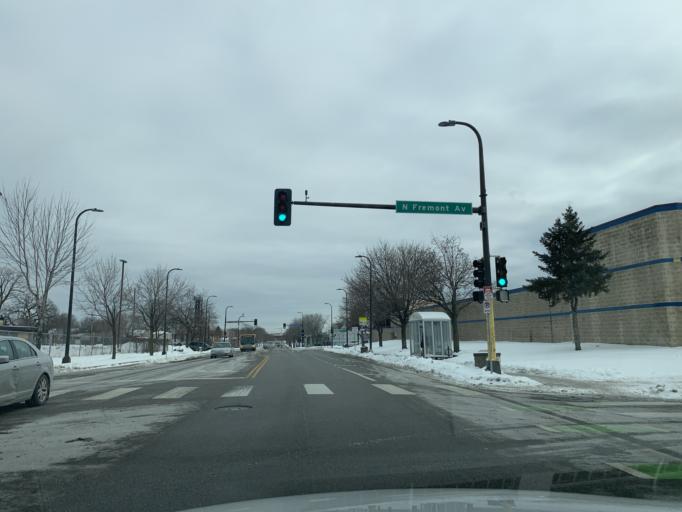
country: US
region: Minnesota
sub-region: Hennepin County
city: Minneapolis
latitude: 44.9920
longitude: -93.2957
